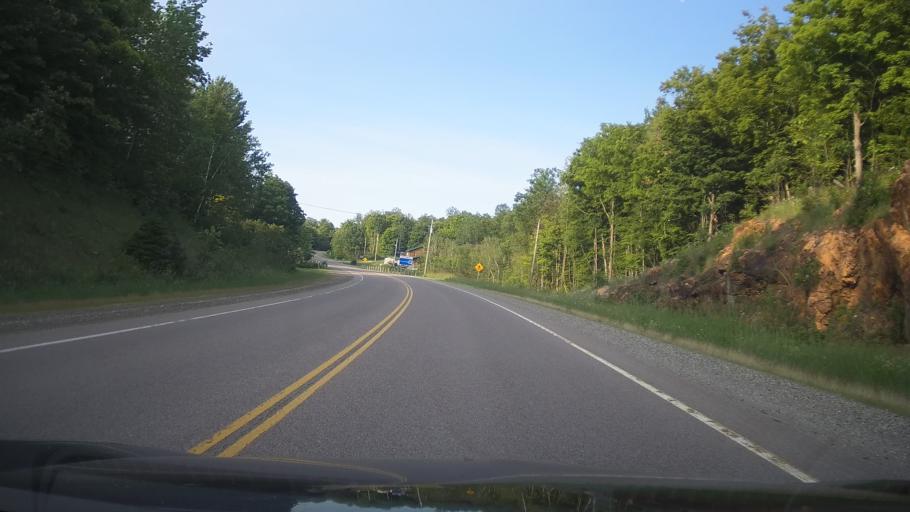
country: CA
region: Ontario
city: Perth
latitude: 44.7814
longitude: -76.7234
